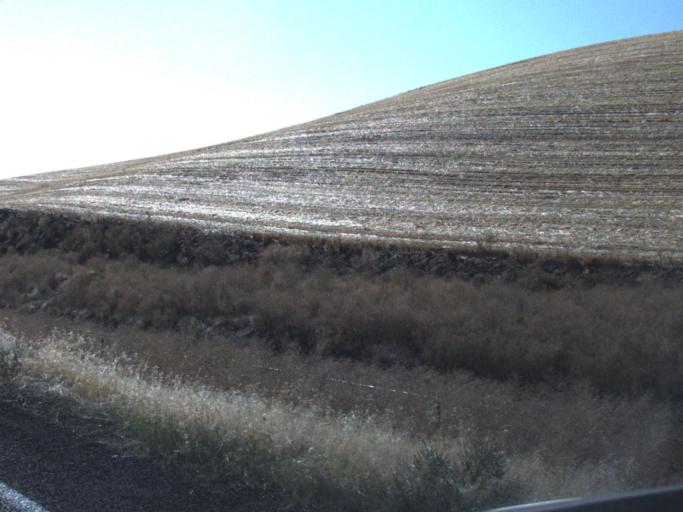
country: US
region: Washington
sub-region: Walla Walla County
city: Waitsburg
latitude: 46.2674
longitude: -118.3511
